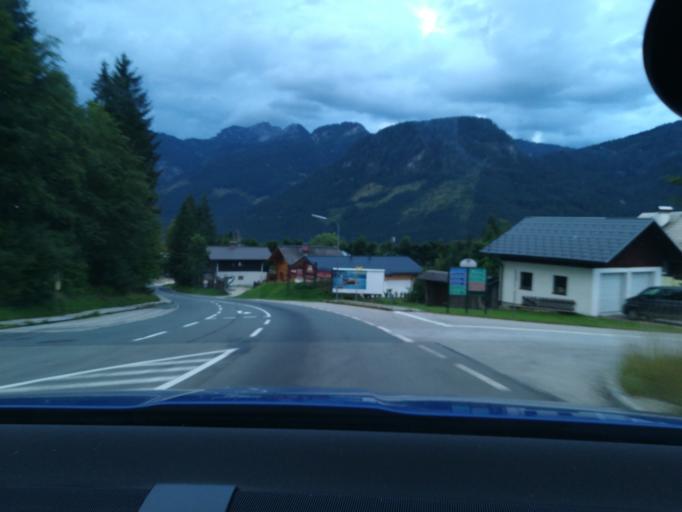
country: AT
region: Upper Austria
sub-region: Politischer Bezirk Gmunden
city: Bad Goisern
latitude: 47.5859
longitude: 13.5255
